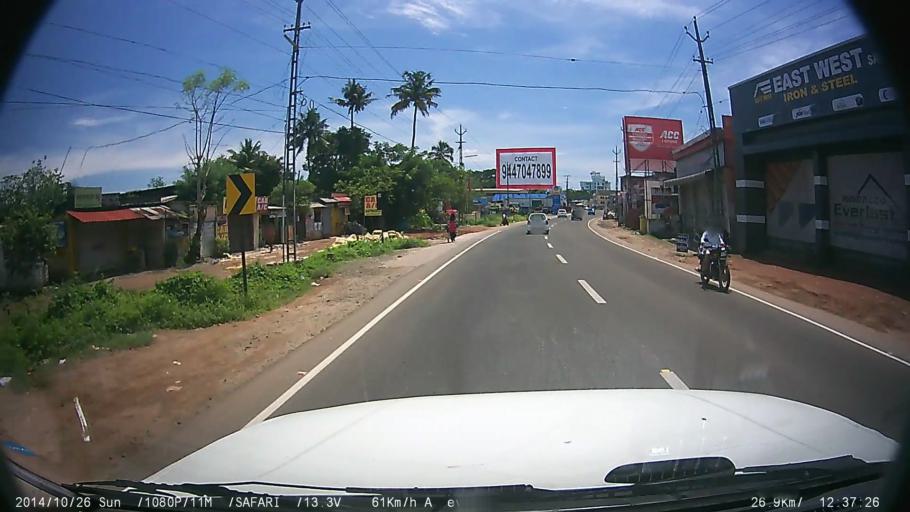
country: IN
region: Kerala
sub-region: Kottayam
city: Kottayam
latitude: 9.5770
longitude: 76.5197
